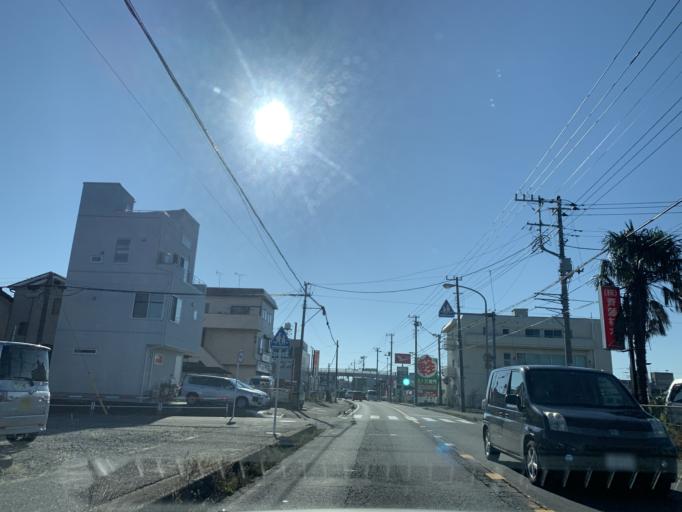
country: JP
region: Chiba
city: Matsudo
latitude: 35.7972
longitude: 139.8965
